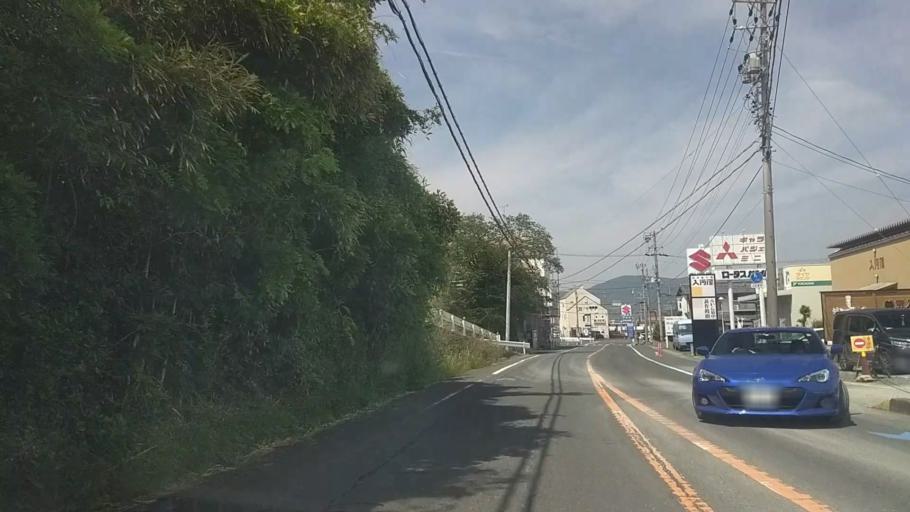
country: JP
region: Shizuoka
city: Kosai-shi
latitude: 34.7923
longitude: 137.5460
